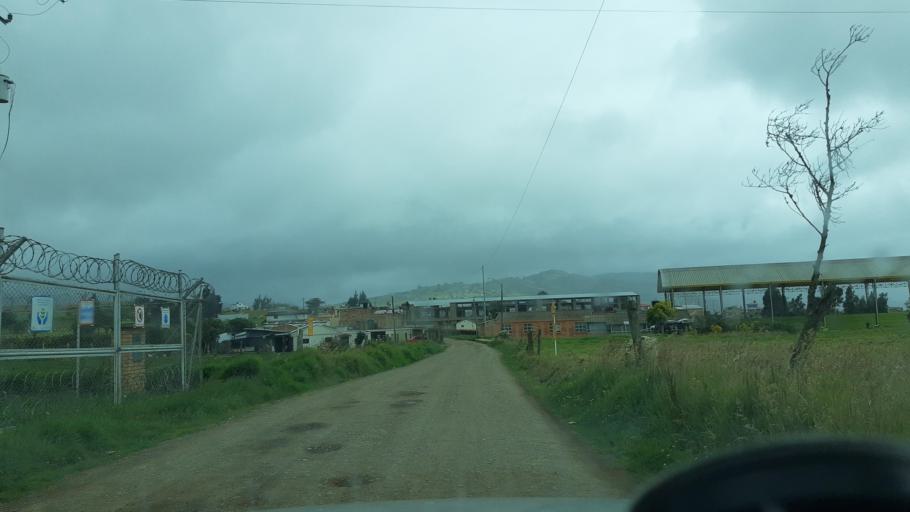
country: CO
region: Boyaca
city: Samaca
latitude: 5.4880
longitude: -73.4646
